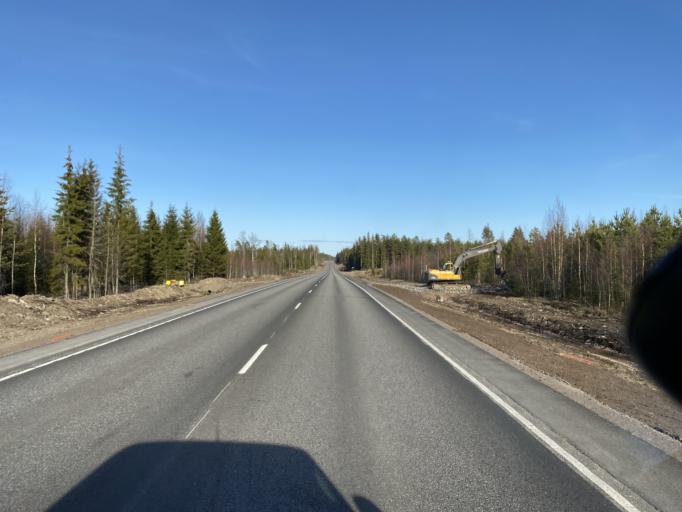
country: FI
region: Satakunta
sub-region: Pori
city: Kokemaeki
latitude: 61.1713
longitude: 22.4876
